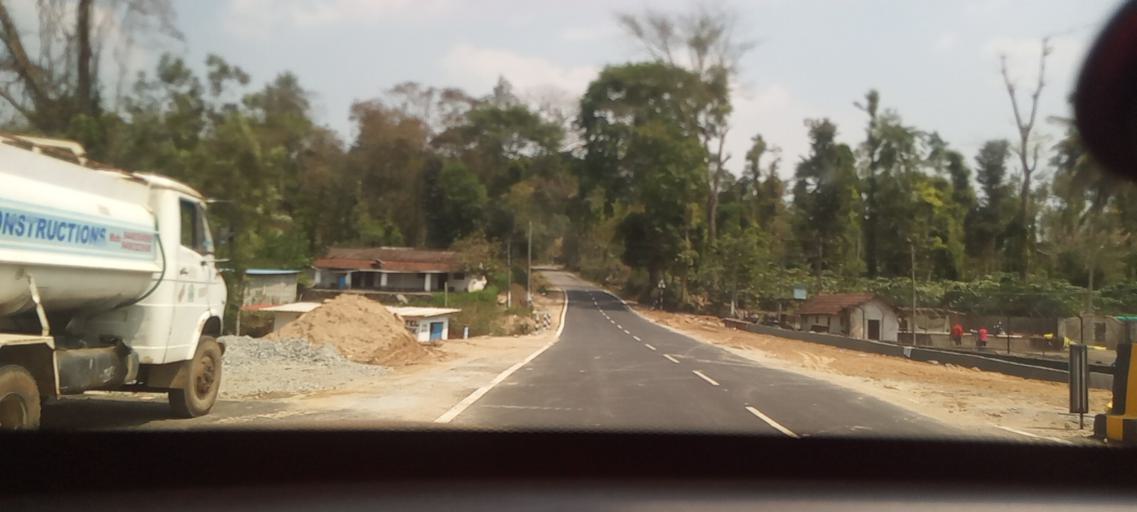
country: IN
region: Karnataka
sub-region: Chikmagalur
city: Mudigere
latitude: 13.2936
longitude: 75.5953
